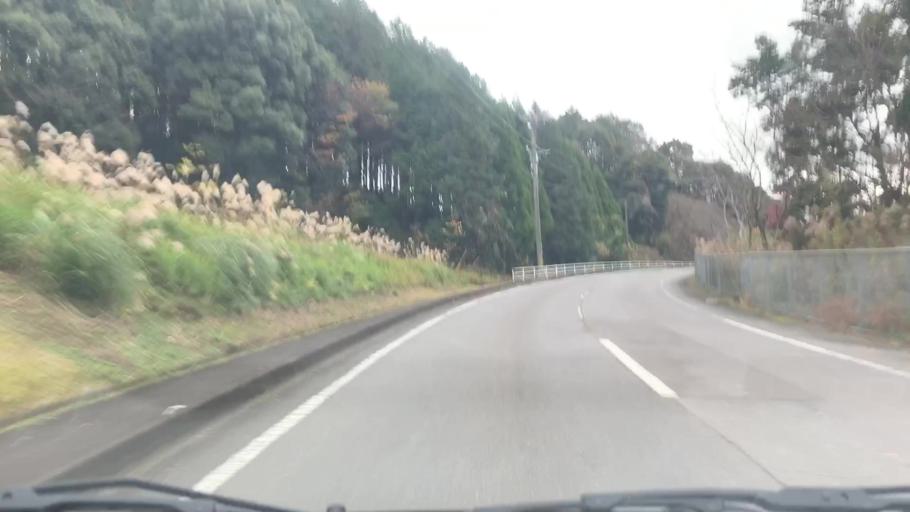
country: JP
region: Saga Prefecture
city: Ureshinomachi-shimojuku
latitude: 33.1119
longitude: 129.9767
